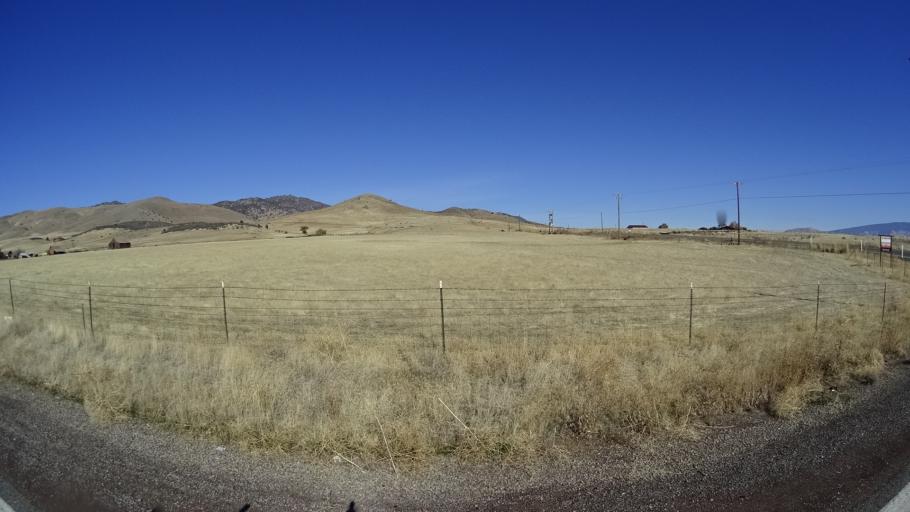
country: US
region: California
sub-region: Siskiyou County
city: Montague
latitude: 41.7714
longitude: -122.5254
